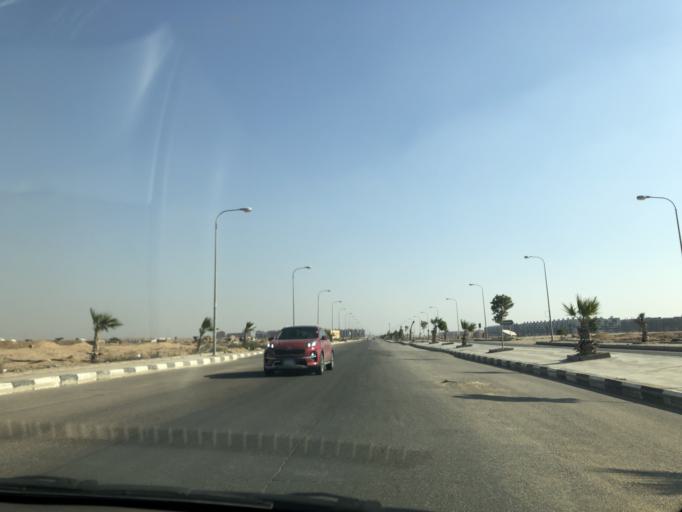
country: EG
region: Al Jizah
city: Madinat Sittah Uktubar
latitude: 29.9154
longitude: 31.0659
